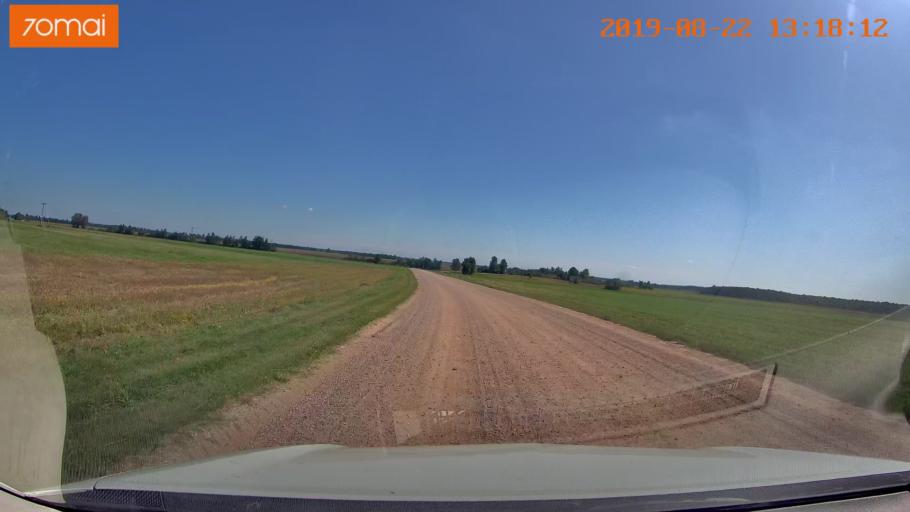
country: BY
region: Minsk
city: Urechcha
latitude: 53.2420
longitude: 27.9343
